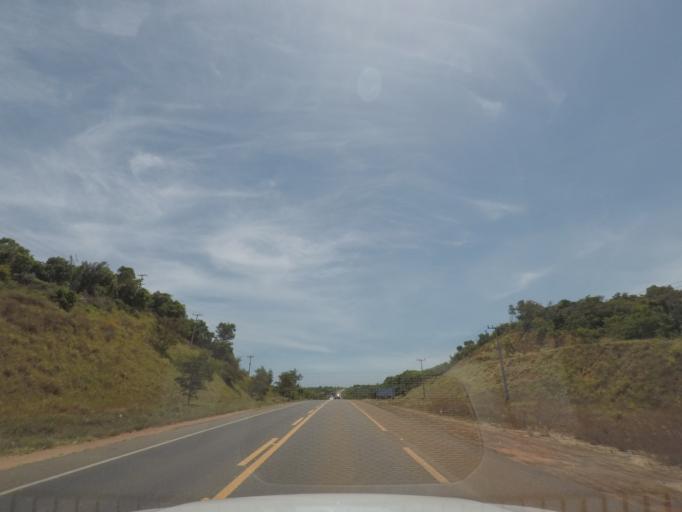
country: BR
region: Bahia
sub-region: Mata De Sao Joao
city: Mata de Sao Joao
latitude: -12.4758
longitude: -37.9625
